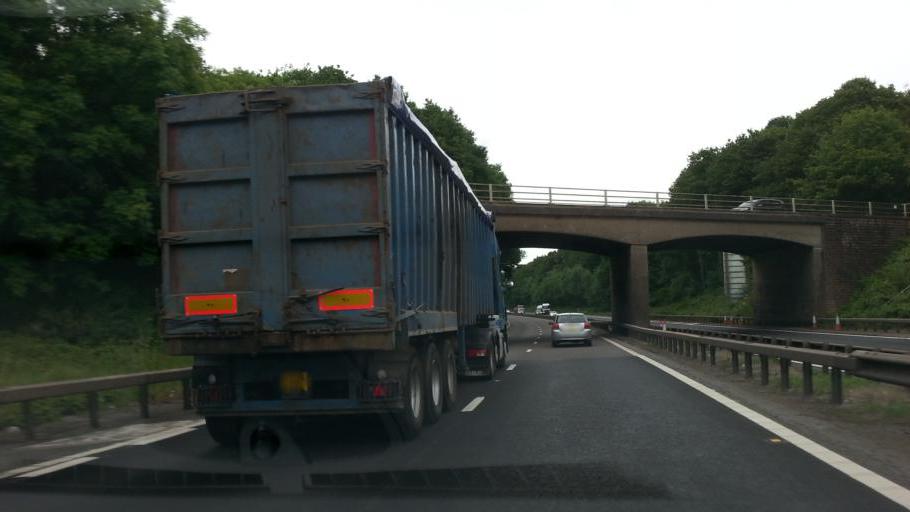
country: GB
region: England
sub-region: Herefordshire
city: Linton
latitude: 51.9339
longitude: -2.4837
